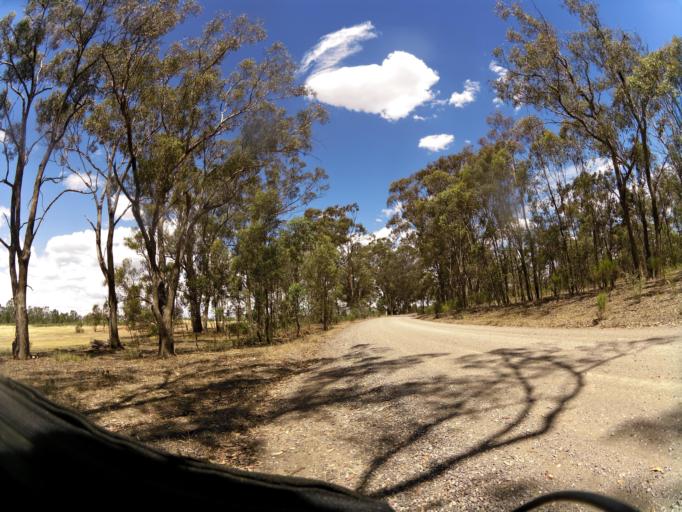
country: AU
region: Victoria
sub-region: Campaspe
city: Kyabram
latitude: -36.8123
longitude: 145.0776
